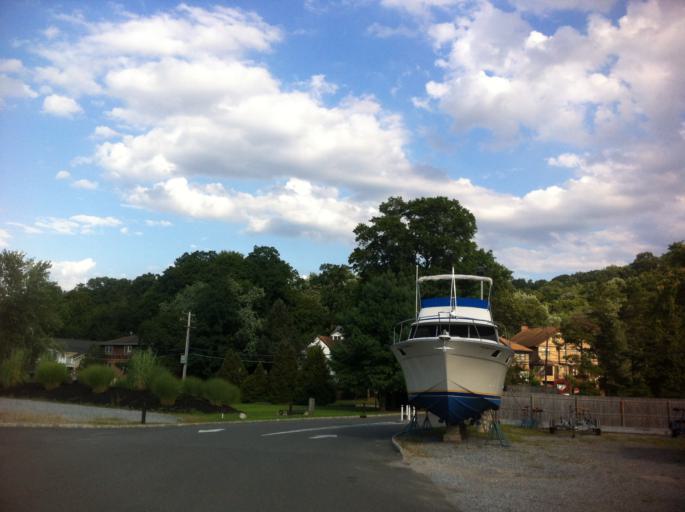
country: US
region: New York
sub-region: Nassau County
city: Sea Cliff
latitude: 40.8555
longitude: -73.6439
